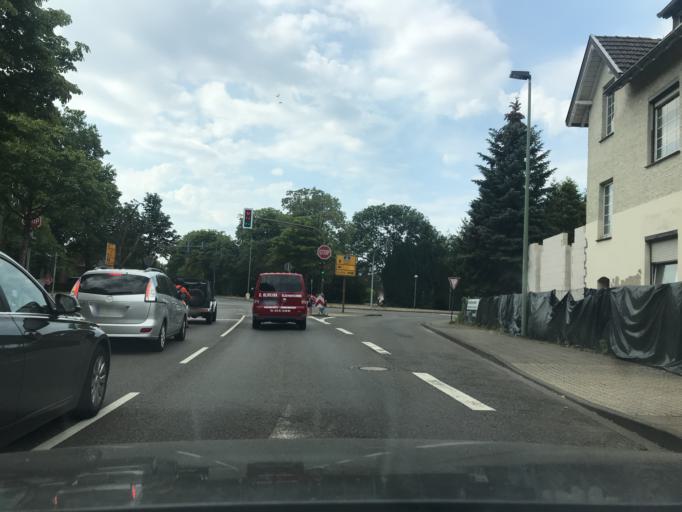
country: DE
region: North Rhine-Westphalia
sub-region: Regierungsbezirk Dusseldorf
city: Kaarst
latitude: 51.2717
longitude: 6.6233
